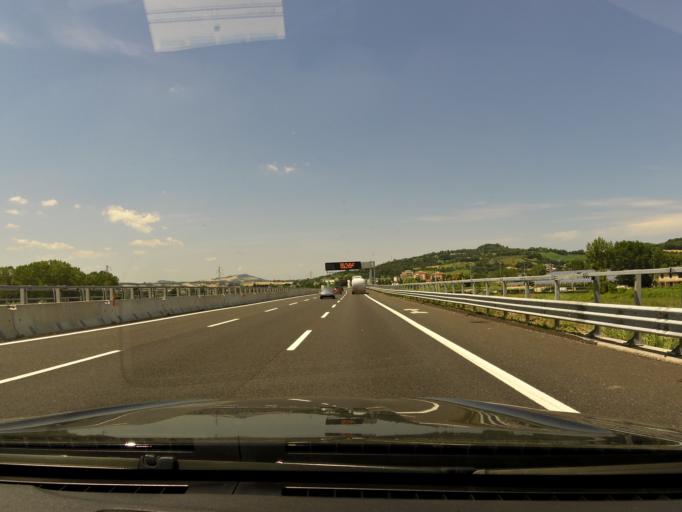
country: IT
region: The Marches
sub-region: Provincia di Pesaro e Urbino
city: Pesaro
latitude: 43.8985
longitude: 12.8695
